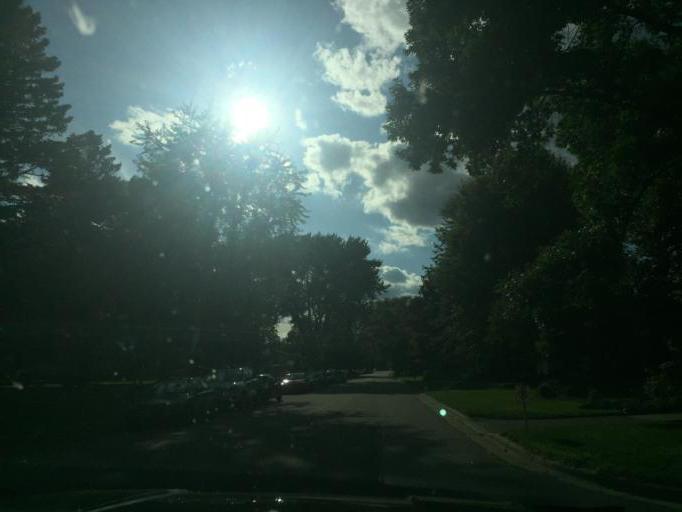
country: US
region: Minnesota
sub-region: Ramsey County
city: Roseville
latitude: 44.9950
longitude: -93.1426
